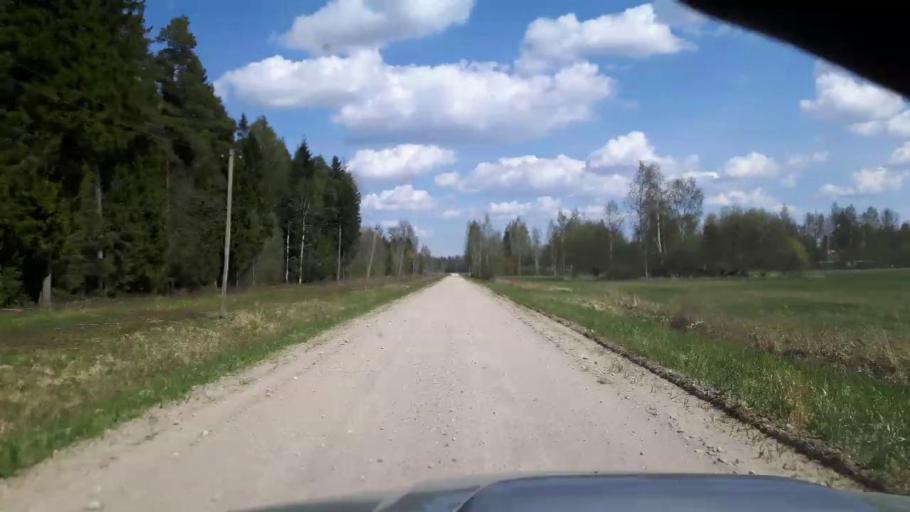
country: EE
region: Paernumaa
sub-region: Tootsi vald
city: Tootsi
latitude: 58.4682
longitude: 24.8948
